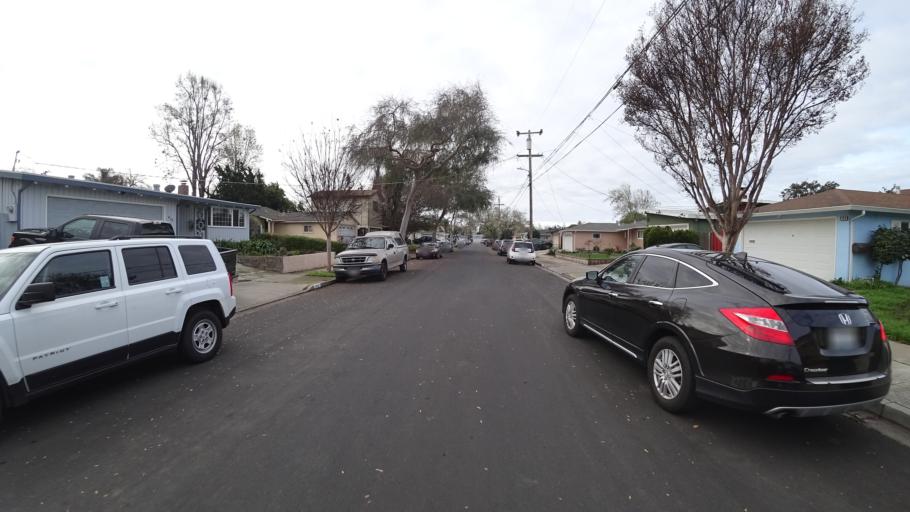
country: US
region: California
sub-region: Alameda County
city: Union City
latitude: 37.6210
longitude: -122.0388
